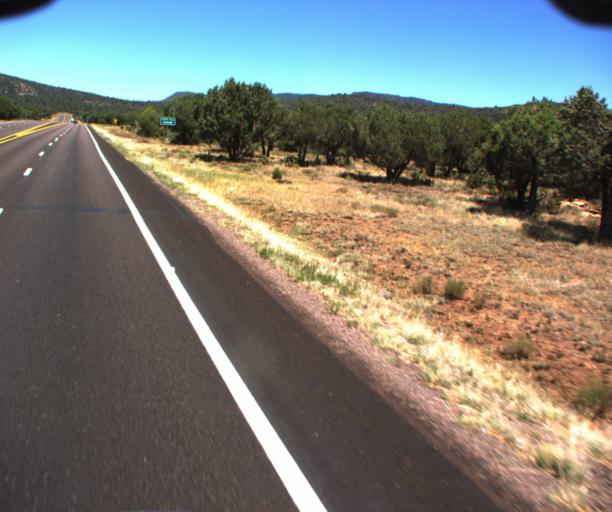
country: US
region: Arizona
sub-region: Gila County
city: Pine
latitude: 34.3300
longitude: -111.4188
